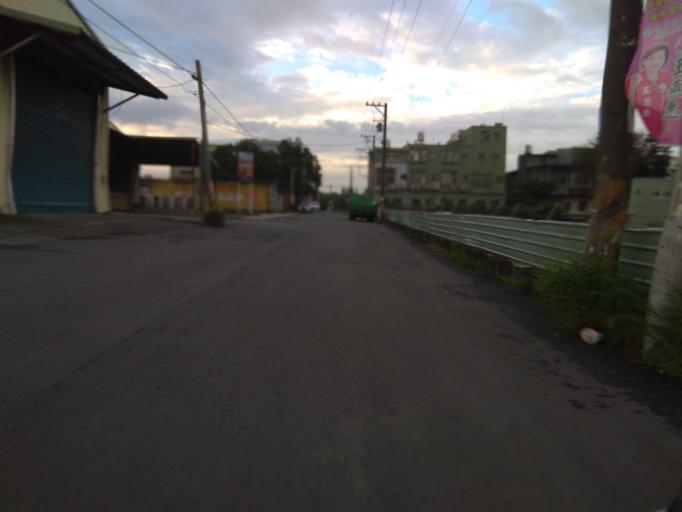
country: TW
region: Taiwan
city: Taoyuan City
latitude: 24.9487
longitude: 121.1927
